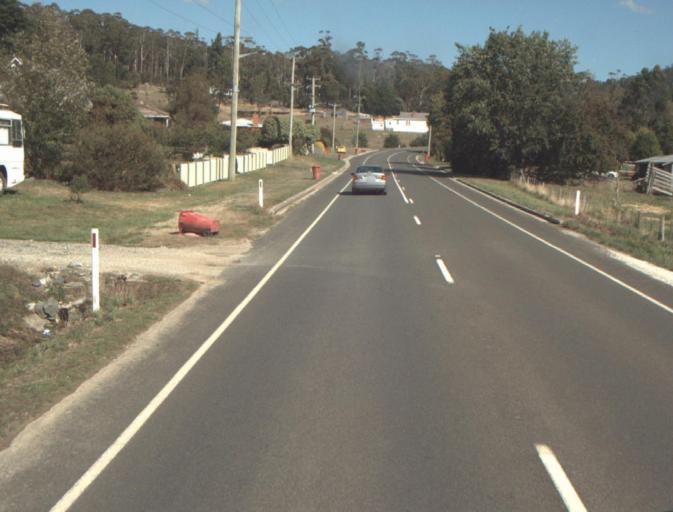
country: AU
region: Tasmania
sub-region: Launceston
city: Mayfield
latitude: -41.2605
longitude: 147.2180
